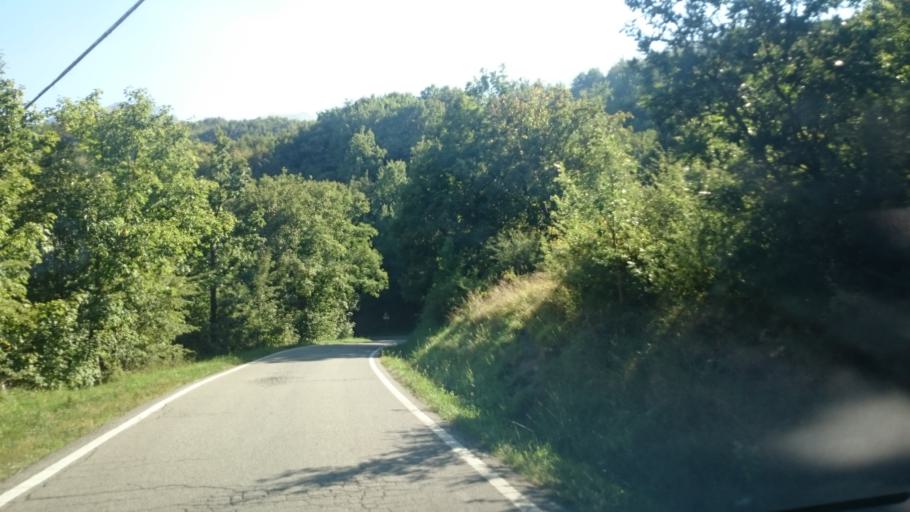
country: IT
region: Emilia-Romagna
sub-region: Provincia di Reggio Emilia
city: Villa Minozzo
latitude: 44.3019
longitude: 10.4346
